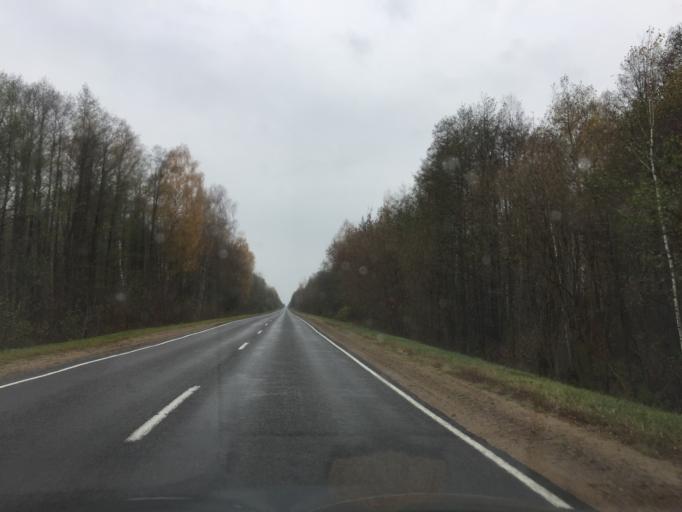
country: BY
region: Mogilev
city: Slawharad
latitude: 53.3646
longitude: 30.8499
